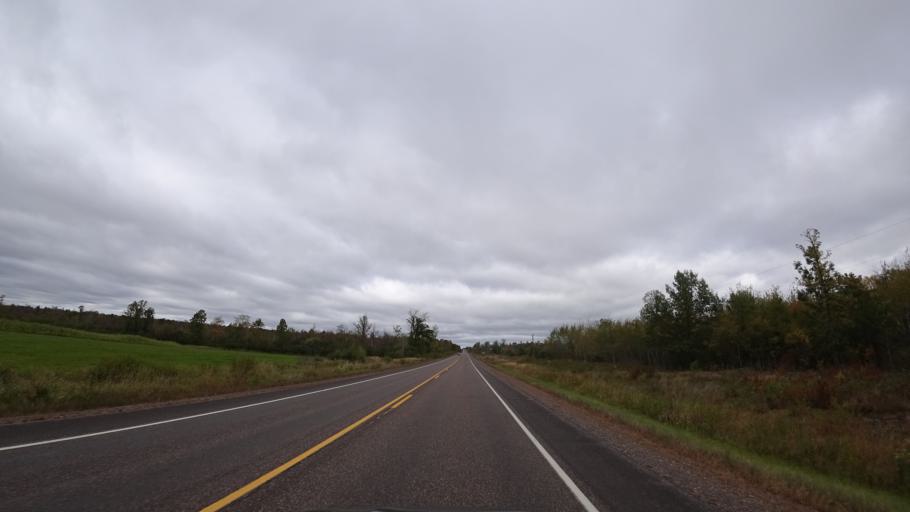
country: US
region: Wisconsin
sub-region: Rusk County
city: Ladysmith
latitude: 45.3846
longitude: -91.1103
